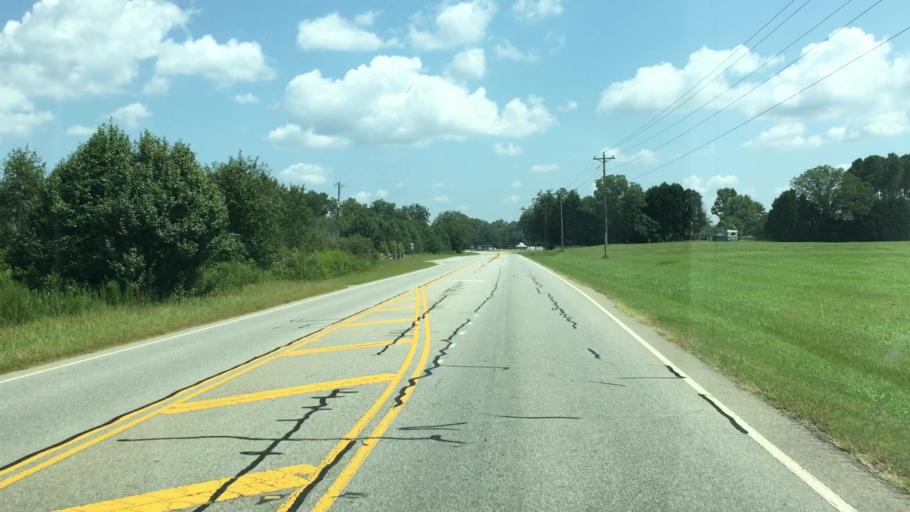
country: US
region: Georgia
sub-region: Oconee County
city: Bogart
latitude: 33.8841
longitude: -83.5541
